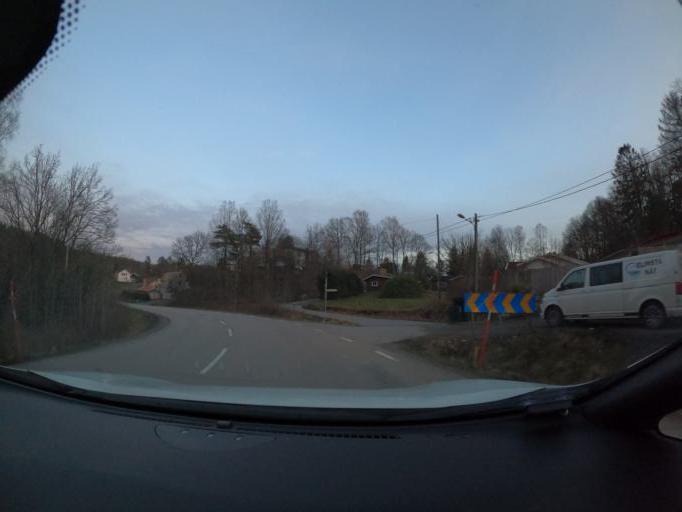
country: SE
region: Vaestra Goetaland
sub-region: Harryda Kommun
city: Molnlycke
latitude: 57.6410
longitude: 12.1724
